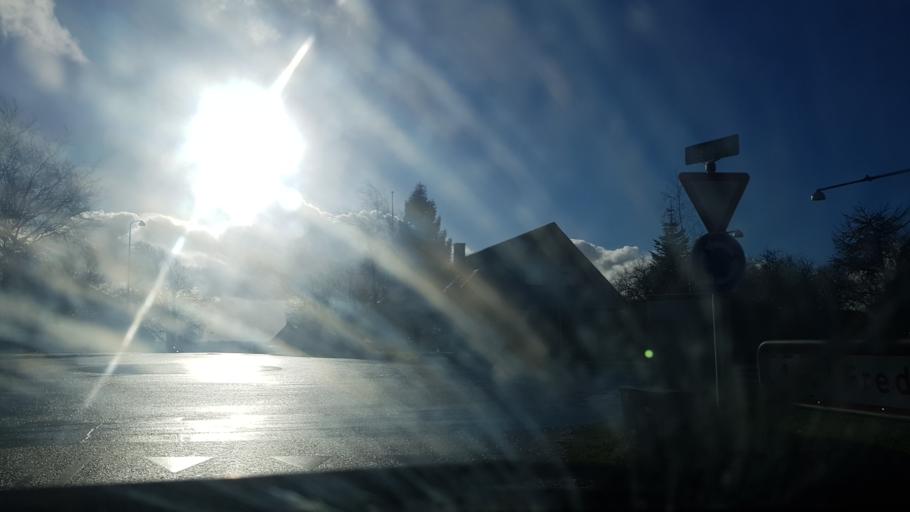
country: DK
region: South Denmark
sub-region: Fredericia Kommune
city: Taulov
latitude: 55.5191
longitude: 9.6348
